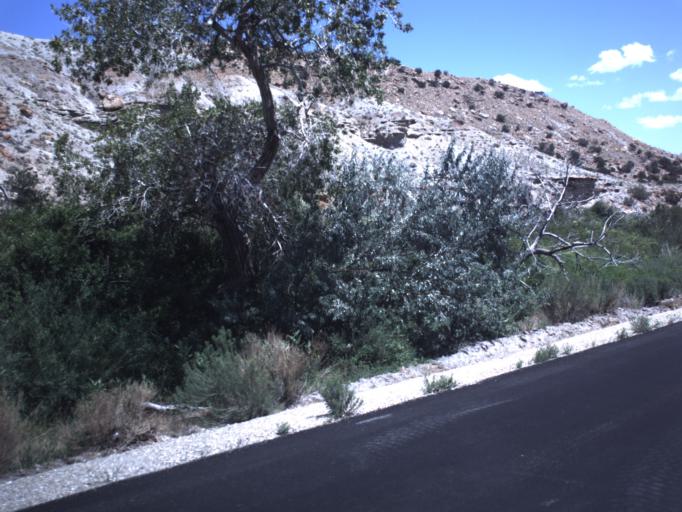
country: US
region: Utah
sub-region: Emery County
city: Orangeville
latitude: 39.2691
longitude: -111.1442
